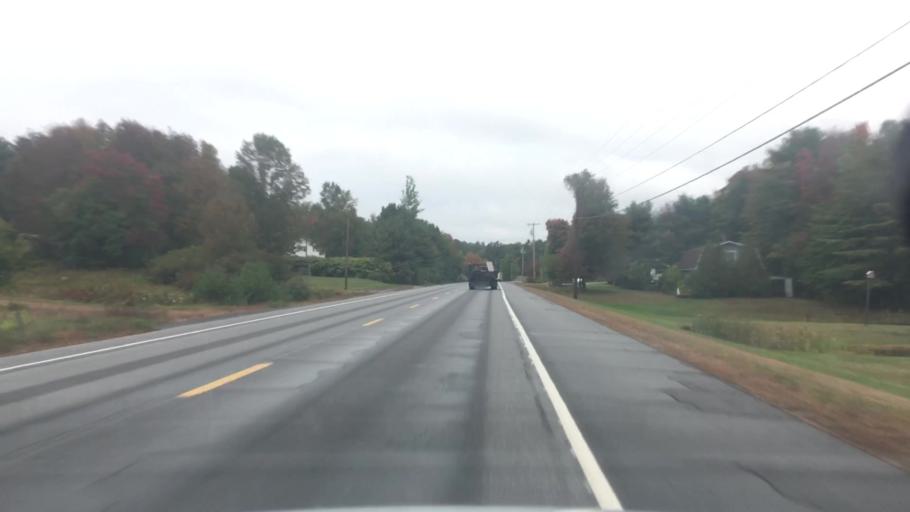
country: US
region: Maine
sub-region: Kennebec County
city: Belgrade
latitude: 44.4308
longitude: -69.8320
